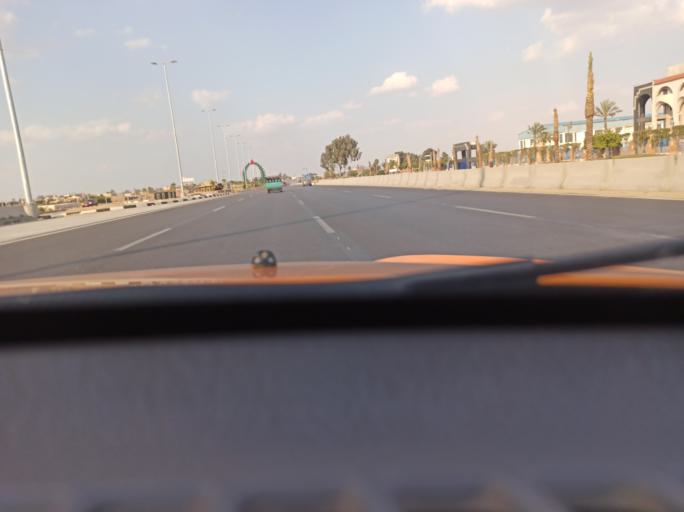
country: EG
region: Al Isma'iliyah
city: Ismailia
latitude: 30.6051
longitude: 32.2122
